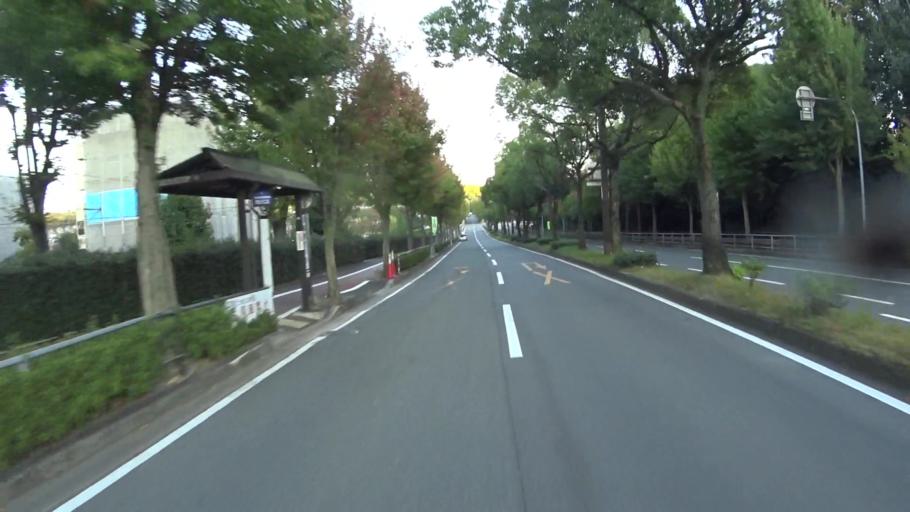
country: JP
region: Kyoto
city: Muko
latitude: 34.9555
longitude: 135.6803
